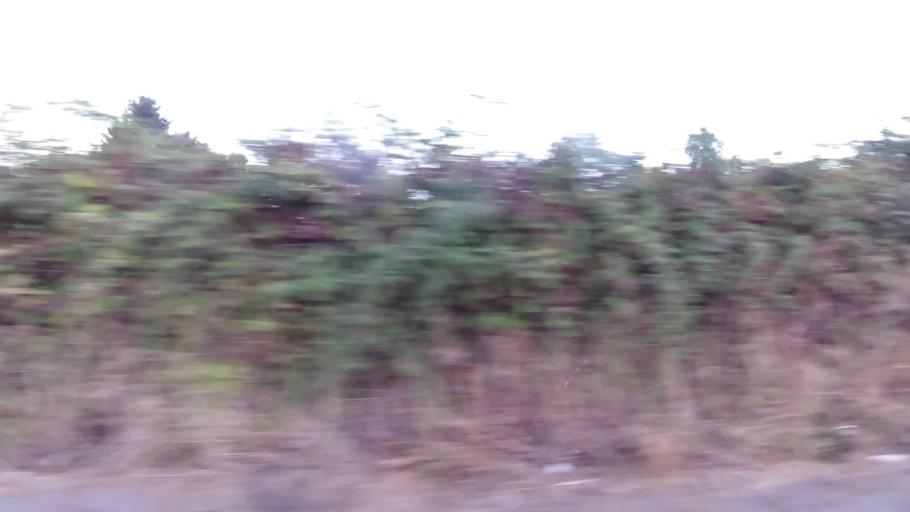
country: CL
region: Maule
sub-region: Provincia de Talca
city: Talca
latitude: -35.4485
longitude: -71.6244
